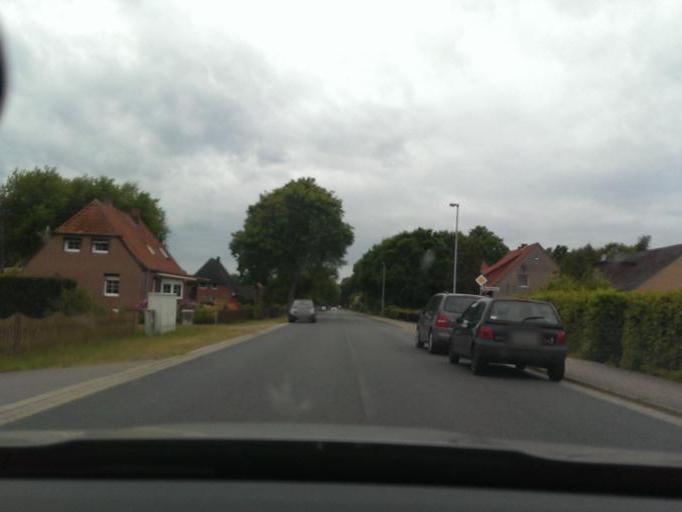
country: DE
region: Lower Saxony
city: Wietze
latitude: 52.6776
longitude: 9.7645
